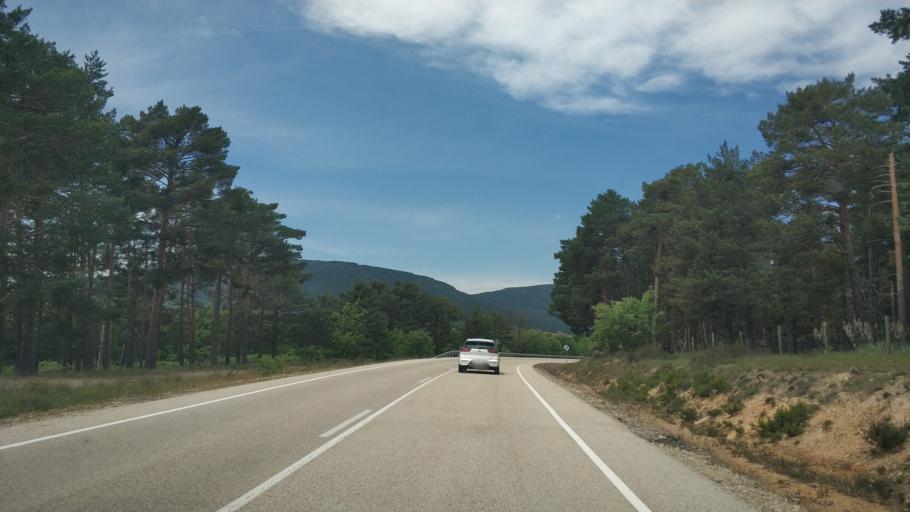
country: ES
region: Castille and Leon
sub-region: Provincia de Soria
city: Vinuesa
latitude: 41.9008
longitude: -2.7381
